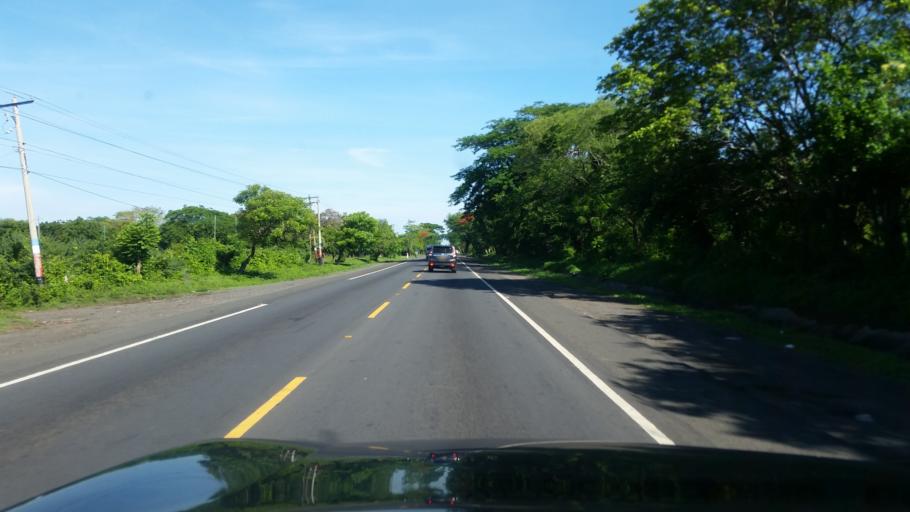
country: NI
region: Leon
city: Quezalguaque
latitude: 12.5383
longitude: -86.9077
